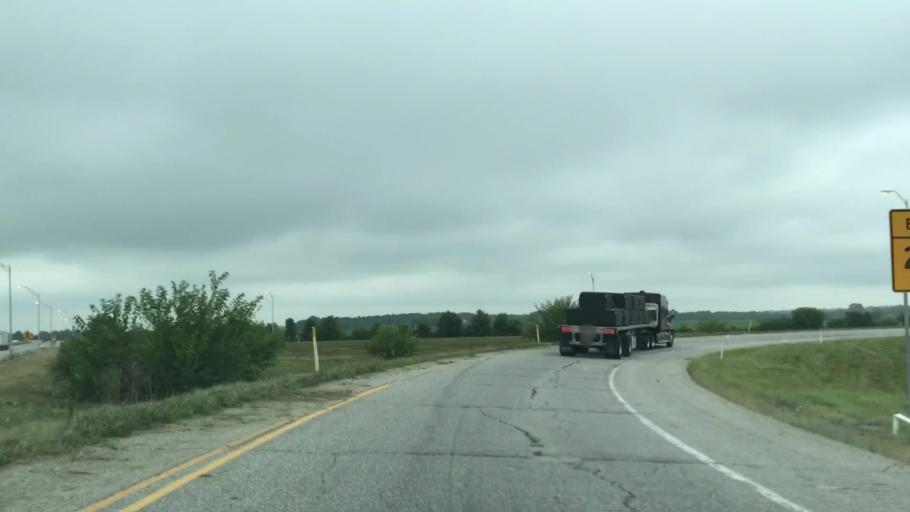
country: US
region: Indiana
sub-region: Tippecanoe County
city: Dayton
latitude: 40.3768
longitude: -86.7843
